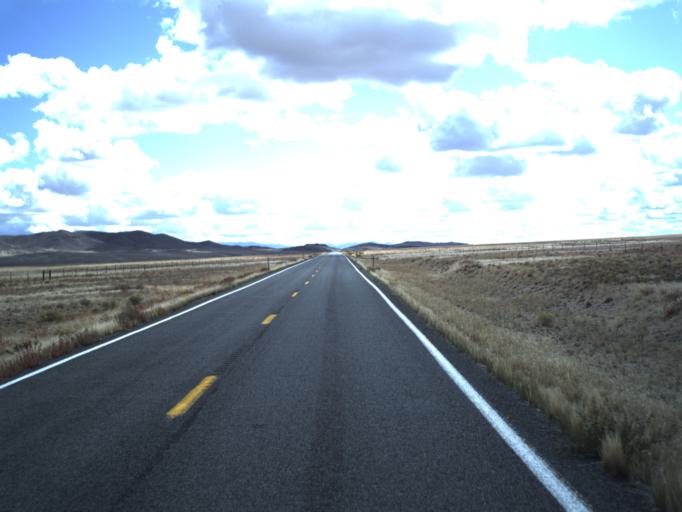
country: US
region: Utah
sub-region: Beaver County
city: Milford
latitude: 38.6792
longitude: -113.8913
